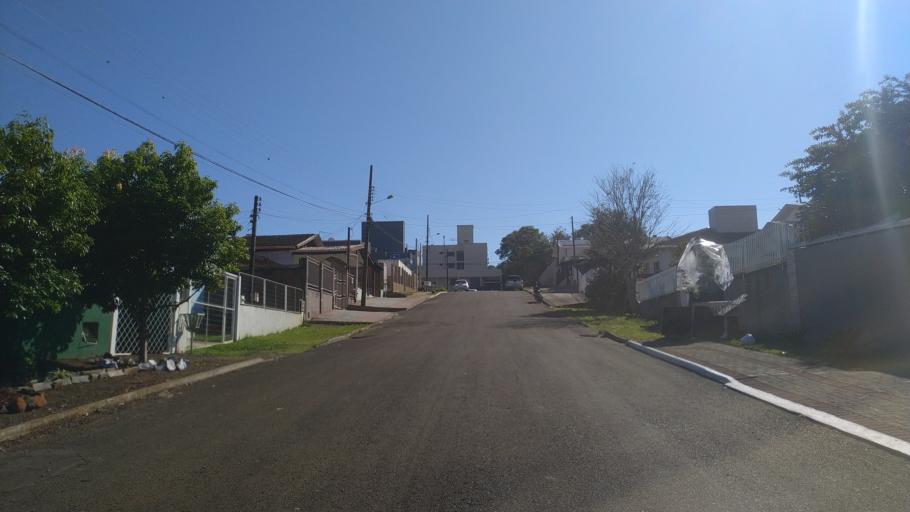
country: BR
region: Santa Catarina
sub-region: Chapeco
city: Chapeco
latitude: -27.1138
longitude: -52.5985
